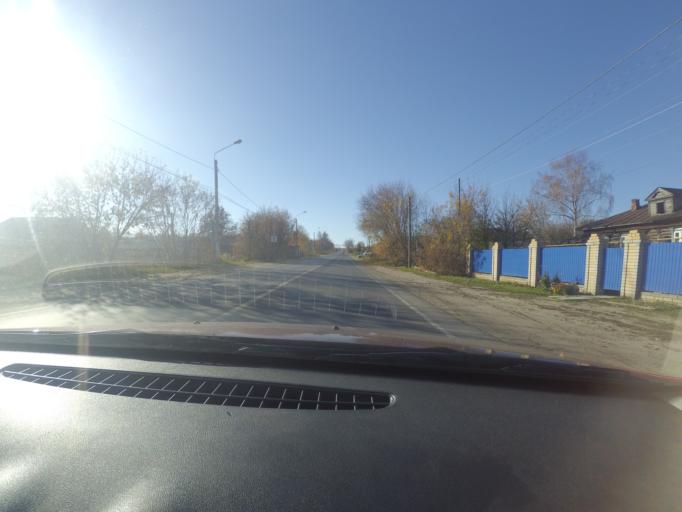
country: RU
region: Nizjnij Novgorod
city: Taremskoye
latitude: 55.9287
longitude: 43.0397
